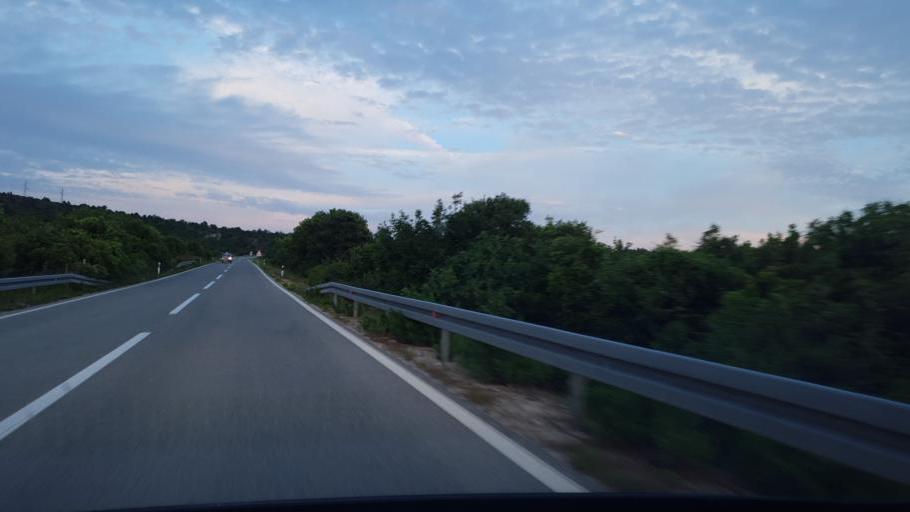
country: HR
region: Primorsko-Goranska
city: Punat
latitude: 45.0335
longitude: 14.6619
